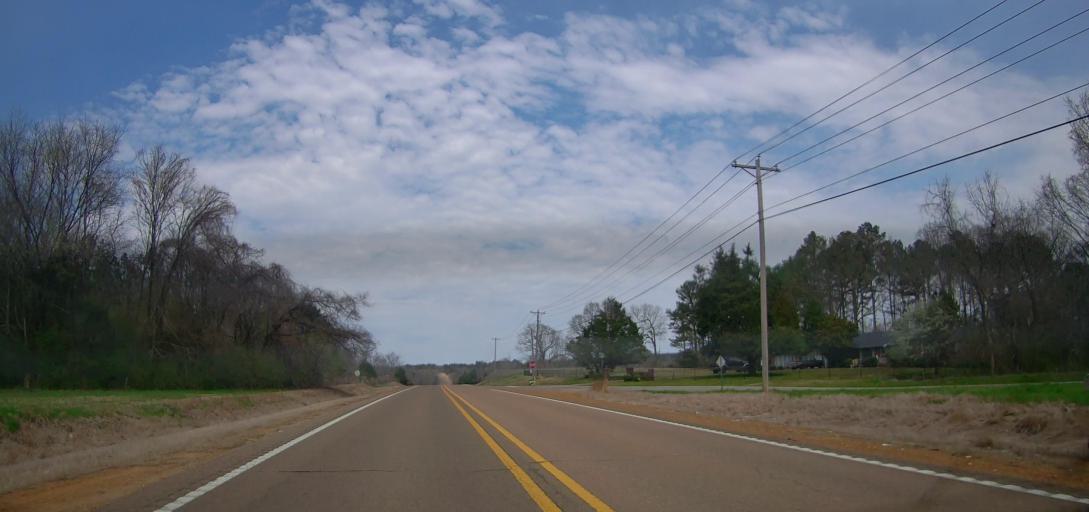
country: US
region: Mississippi
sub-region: Marshall County
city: Holly Springs
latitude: 34.7378
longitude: -89.4236
